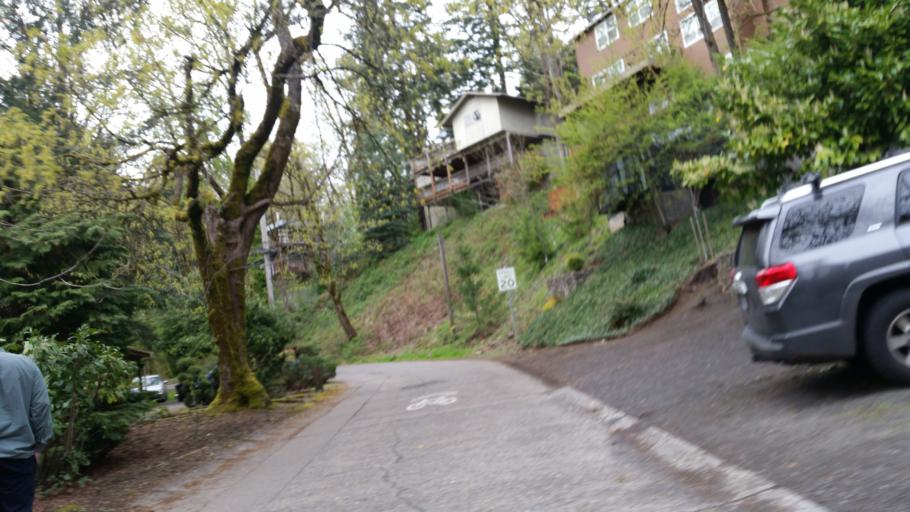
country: US
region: Oregon
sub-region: Multnomah County
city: Portland
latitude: 45.4822
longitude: -122.6868
